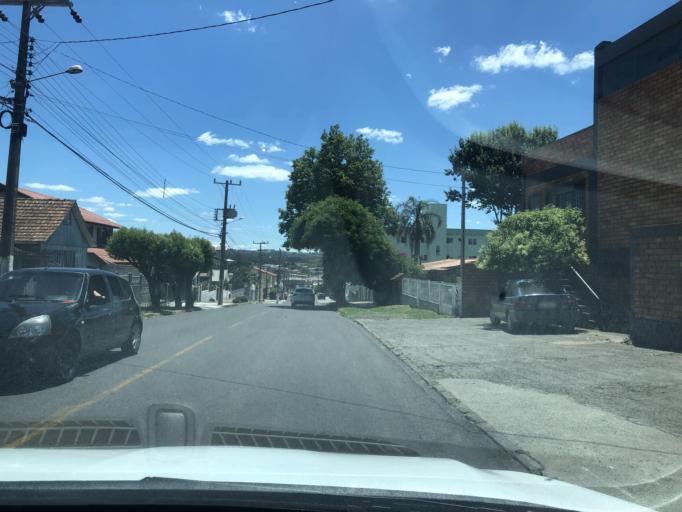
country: BR
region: Santa Catarina
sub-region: Lages
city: Lages
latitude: -27.7964
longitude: -50.3064
